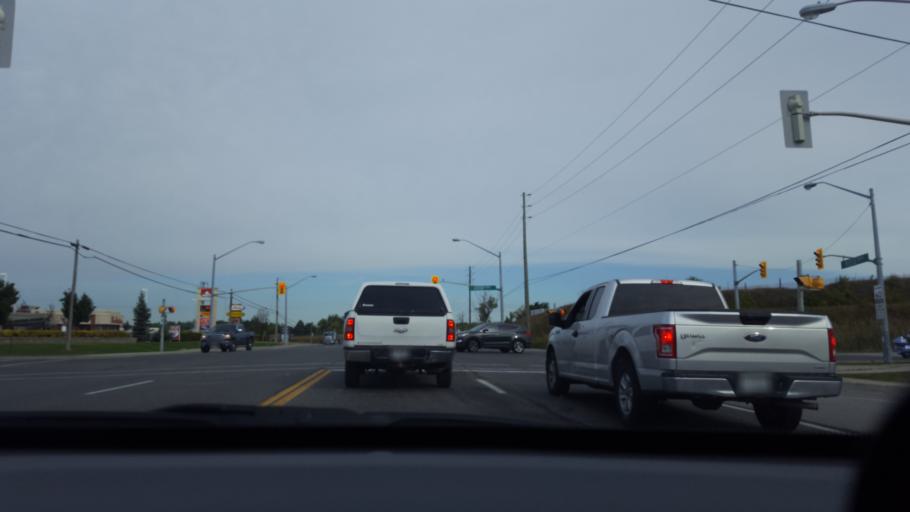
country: CA
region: Ontario
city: Vaughan
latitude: 43.8914
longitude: -79.5209
